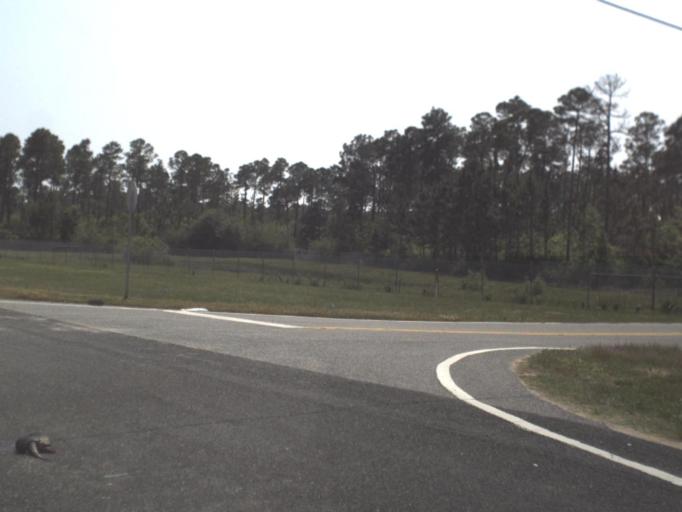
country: US
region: Florida
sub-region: Santa Rosa County
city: Bagdad
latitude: 30.5223
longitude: -87.0873
